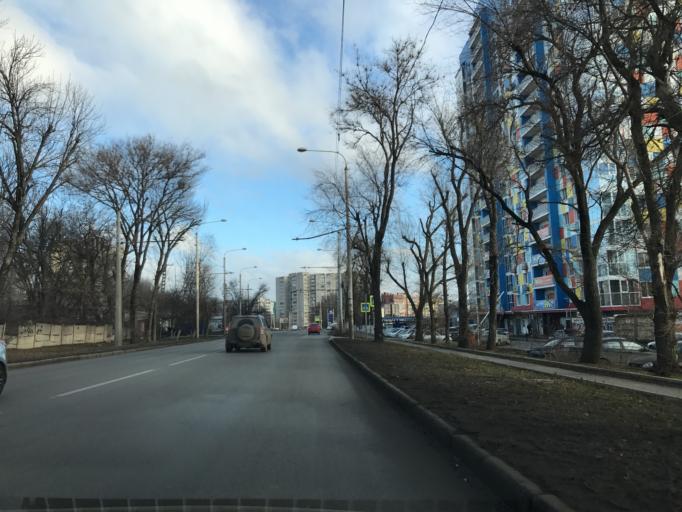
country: RU
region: Rostov
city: Severnyy
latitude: 47.2575
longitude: 39.6372
